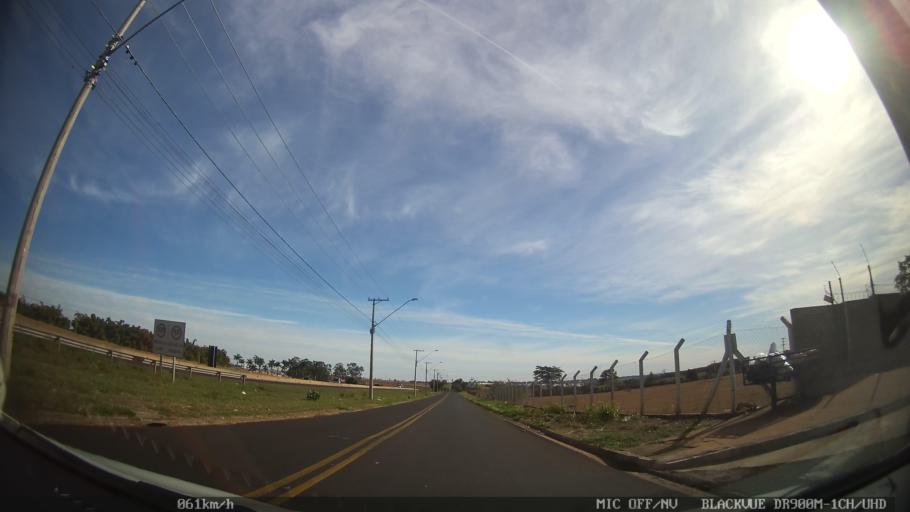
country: BR
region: Sao Paulo
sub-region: Sao Jose Do Rio Preto
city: Sao Jose do Rio Preto
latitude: -20.7935
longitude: -49.3093
